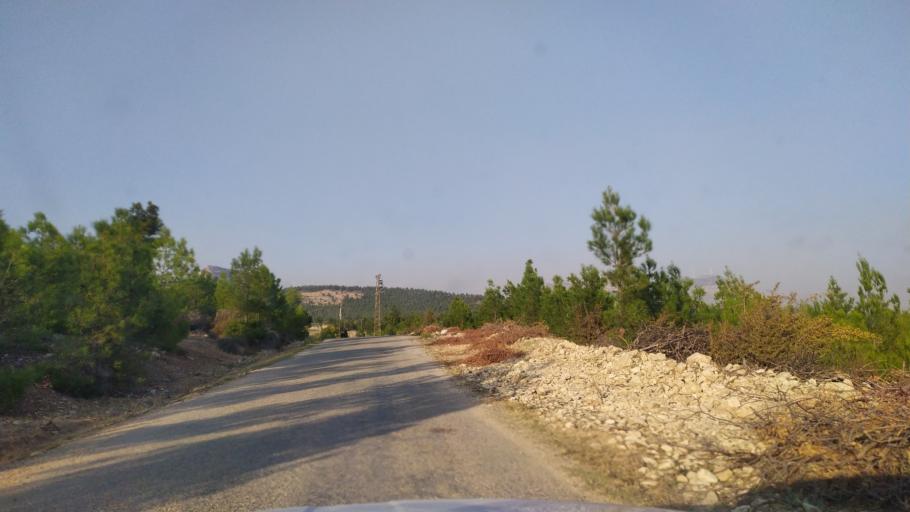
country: TR
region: Mersin
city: Mut
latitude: 36.6852
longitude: 33.1943
